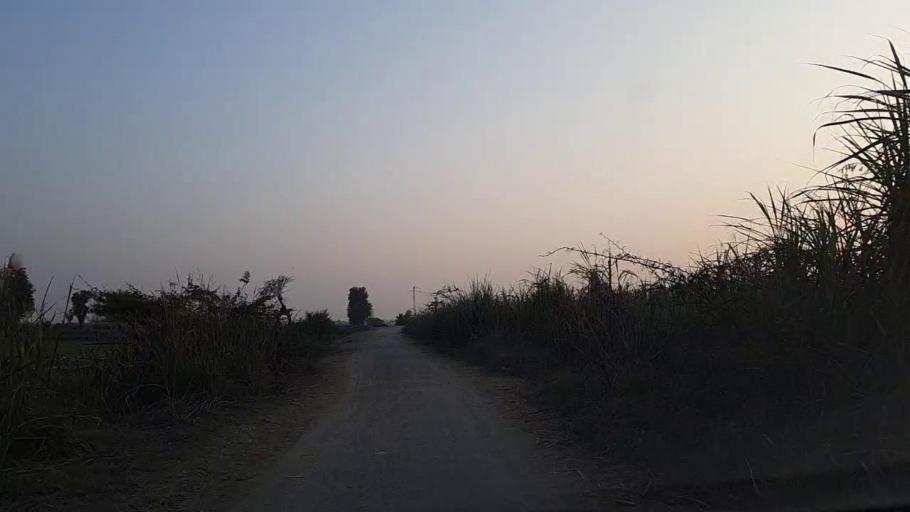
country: PK
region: Sindh
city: Daur
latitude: 26.4424
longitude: 68.3491
